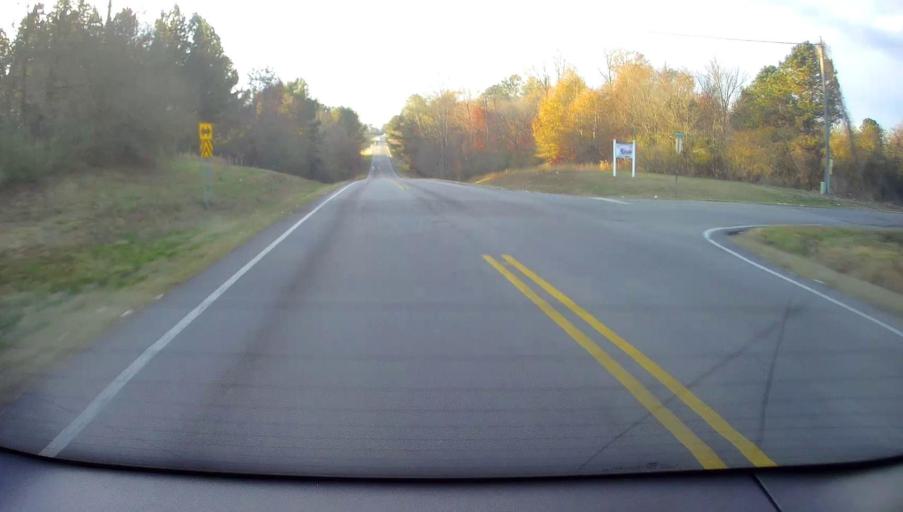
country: US
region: Alabama
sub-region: Blount County
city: Blountsville
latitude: 34.1357
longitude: -86.4267
